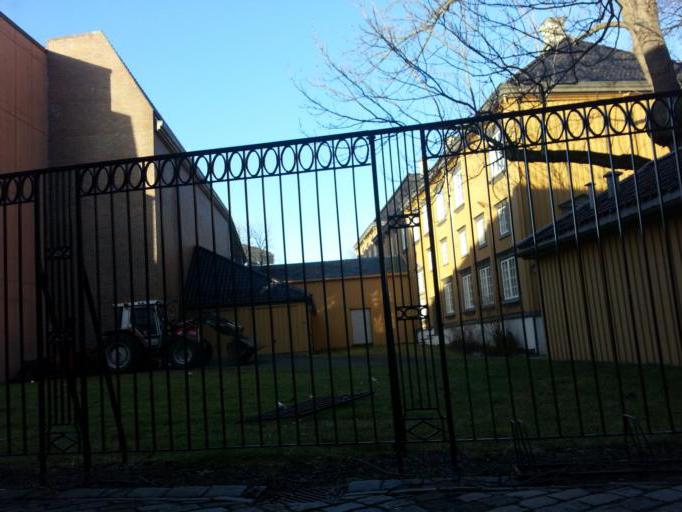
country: NO
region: Sor-Trondelag
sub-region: Trondheim
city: Trondheim
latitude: 63.4312
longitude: 10.3962
